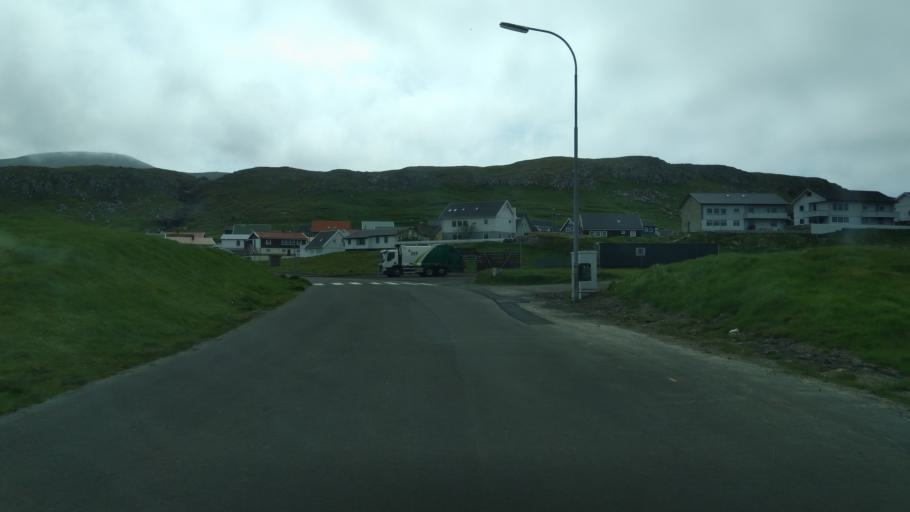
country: FO
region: Sandoy
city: Sandur
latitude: 61.9045
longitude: -6.8874
